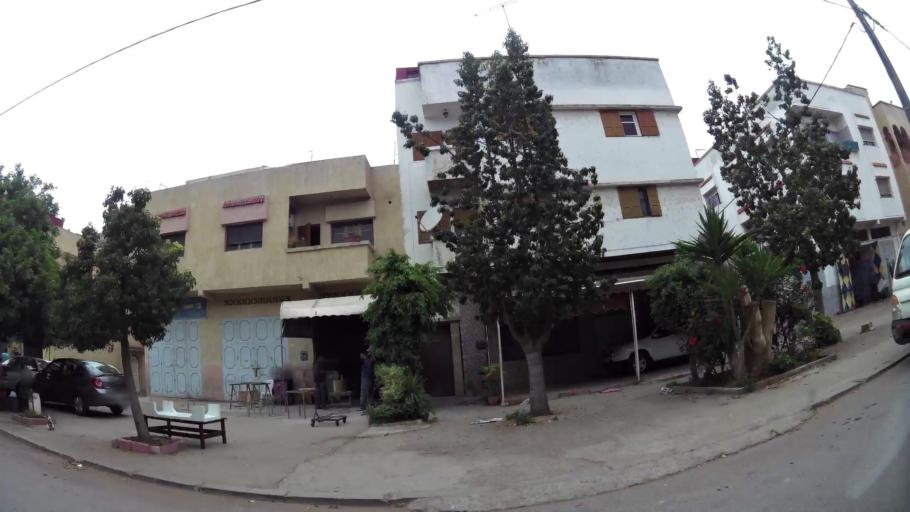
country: MA
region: Rabat-Sale-Zemmour-Zaer
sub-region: Rabat
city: Rabat
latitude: 33.9793
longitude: -6.8167
